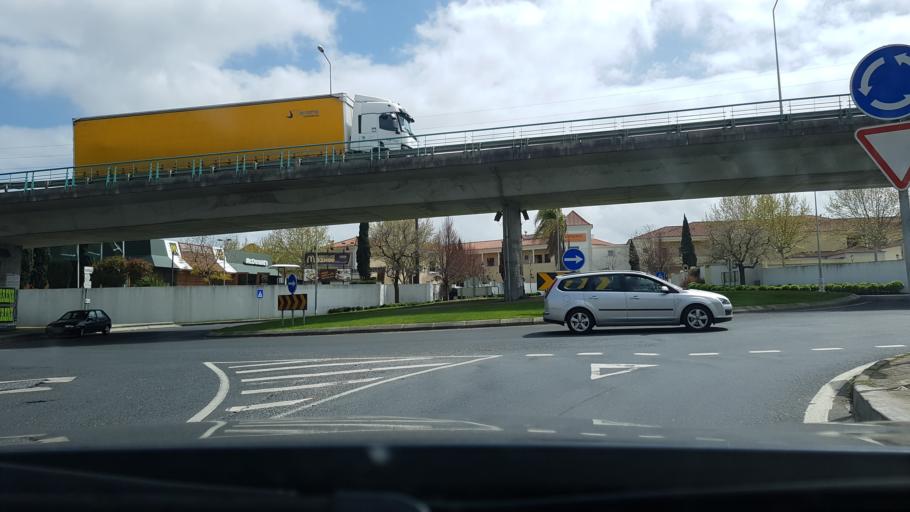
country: PT
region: Lisbon
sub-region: Alenquer
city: Carregado
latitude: 39.0294
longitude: -8.9663
